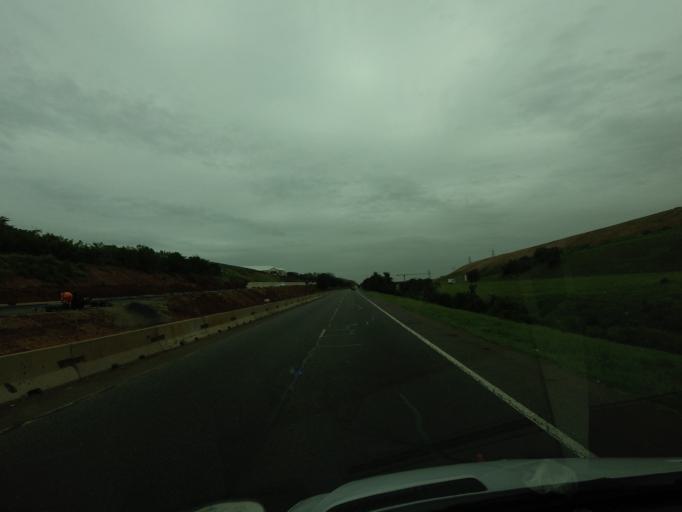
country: ZA
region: KwaZulu-Natal
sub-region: eThekwini Metropolitan Municipality
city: Durban
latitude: -29.7088
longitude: 31.0672
